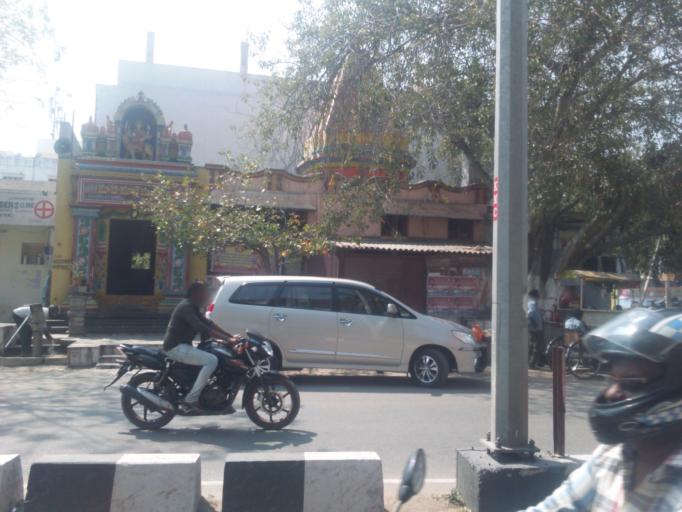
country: IN
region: Telangana
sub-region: Mahbubnagar
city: Alampur
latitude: 15.8398
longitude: 78.0377
